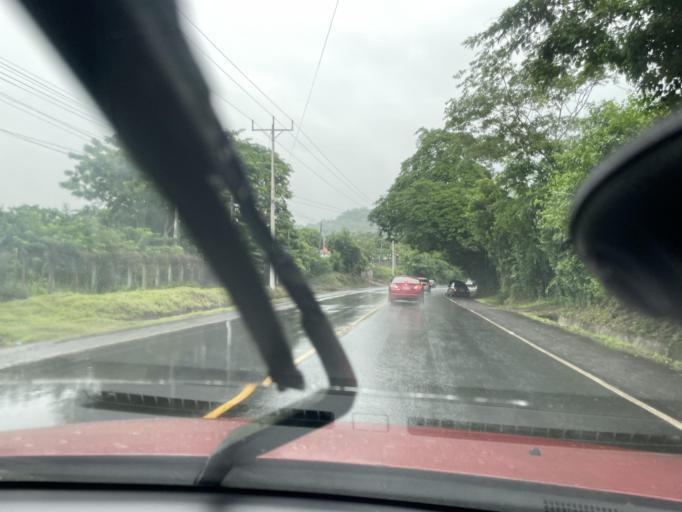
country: SV
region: San Miguel
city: San Miguel
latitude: 13.5493
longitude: -88.1176
